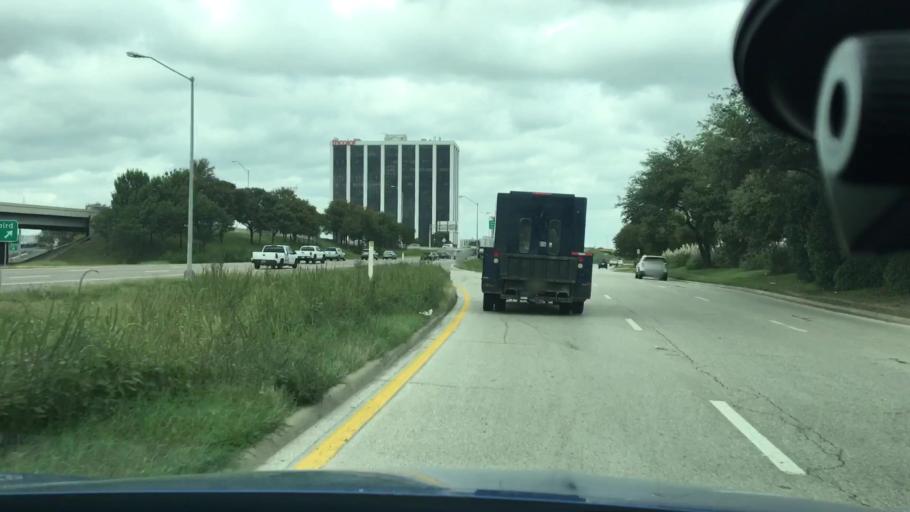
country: US
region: Texas
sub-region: Dallas County
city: Dallas
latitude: 32.8159
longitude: -96.8671
